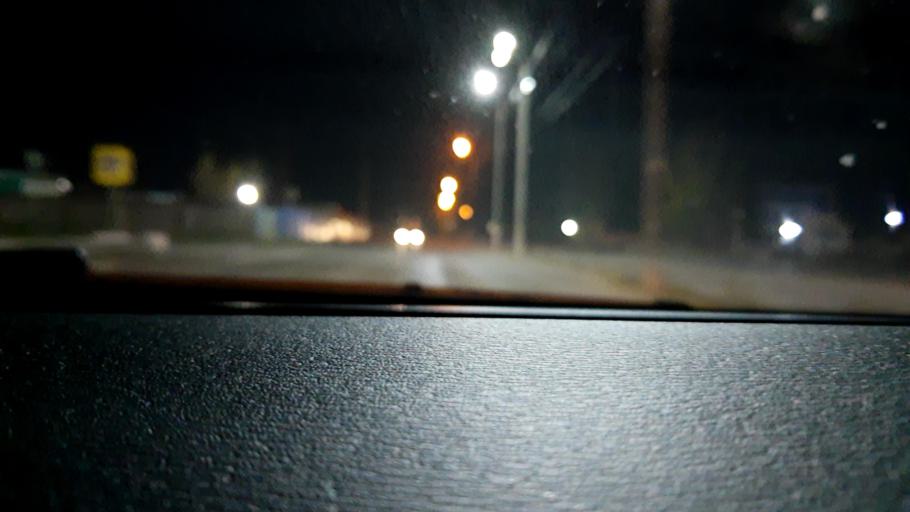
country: RU
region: Nizjnij Novgorod
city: Gorbatovka
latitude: 56.3650
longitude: 43.7947
